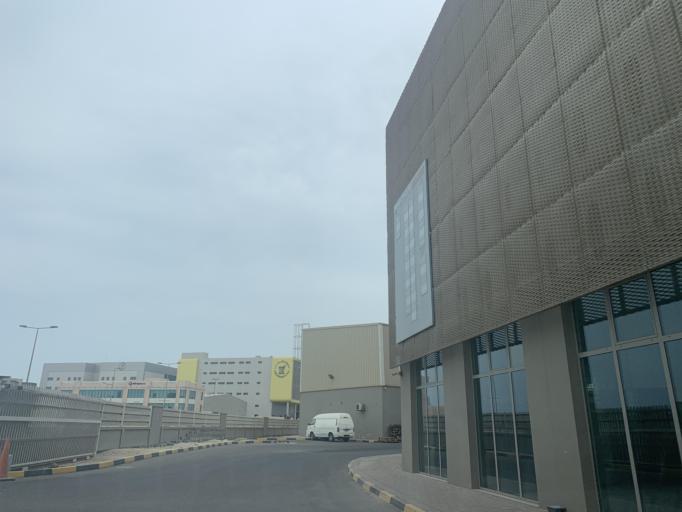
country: BH
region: Muharraq
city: Al Hadd
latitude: 26.2129
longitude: 50.6689
